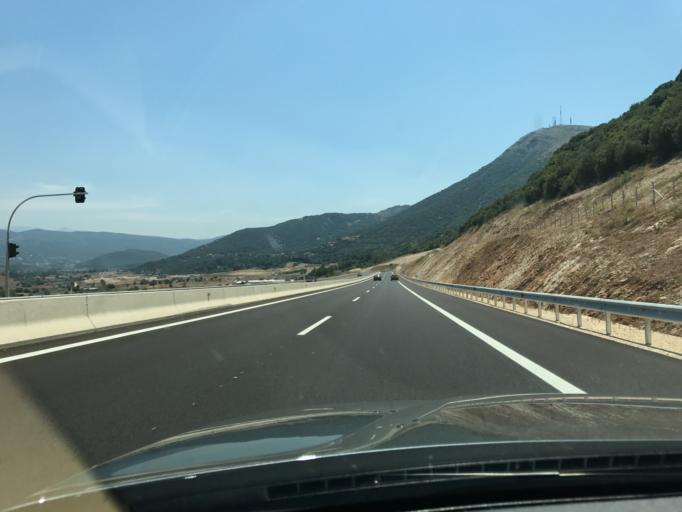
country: GR
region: Epirus
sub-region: Nomos Ioanninon
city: Pedini
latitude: 39.5548
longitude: 20.8361
